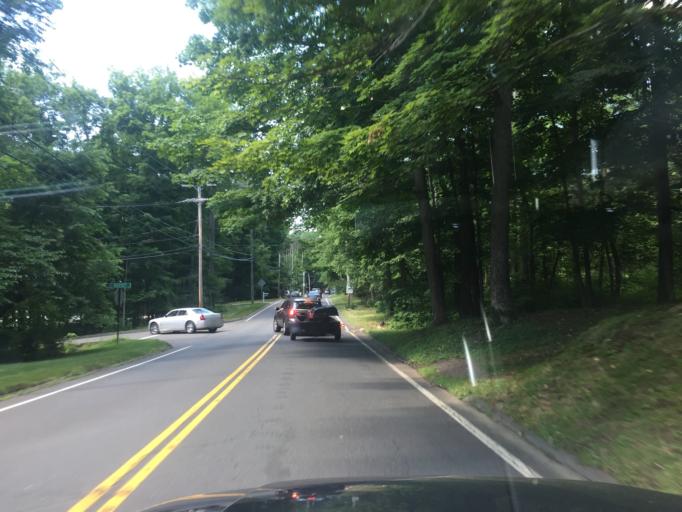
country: US
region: Connecticut
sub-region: Hartford County
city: Farmington
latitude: 41.7540
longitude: -72.8151
